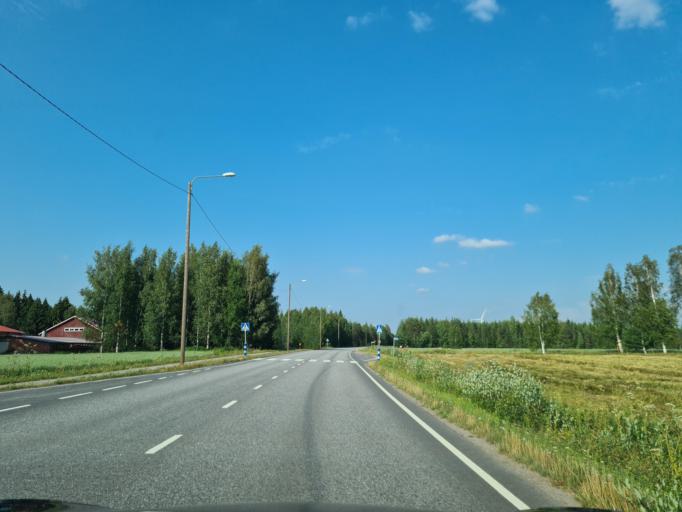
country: FI
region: Satakunta
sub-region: Pohjois-Satakunta
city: Karvia
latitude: 62.0782
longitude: 22.5157
